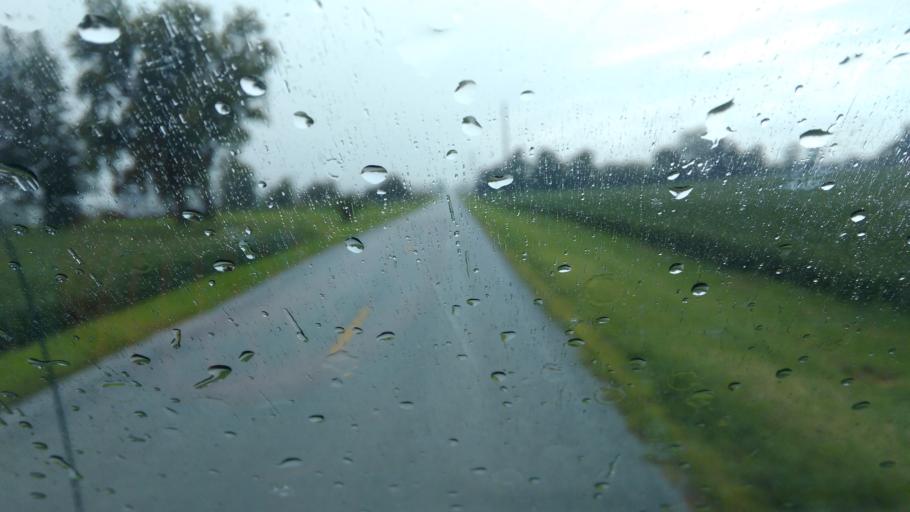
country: US
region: Ohio
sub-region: Hardin County
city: Kenton
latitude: 40.7173
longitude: -83.5828
